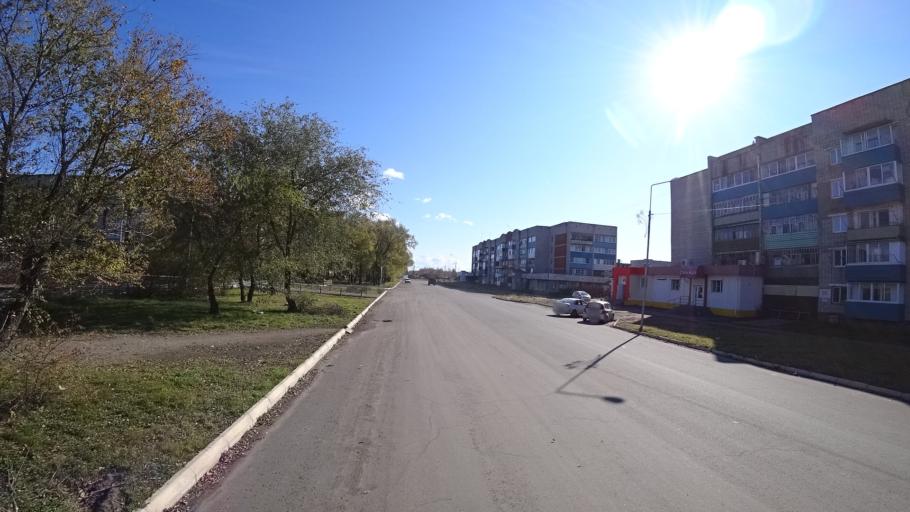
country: RU
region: Khabarovsk Krai
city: Amursk
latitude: 50.0997
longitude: 136.5149
